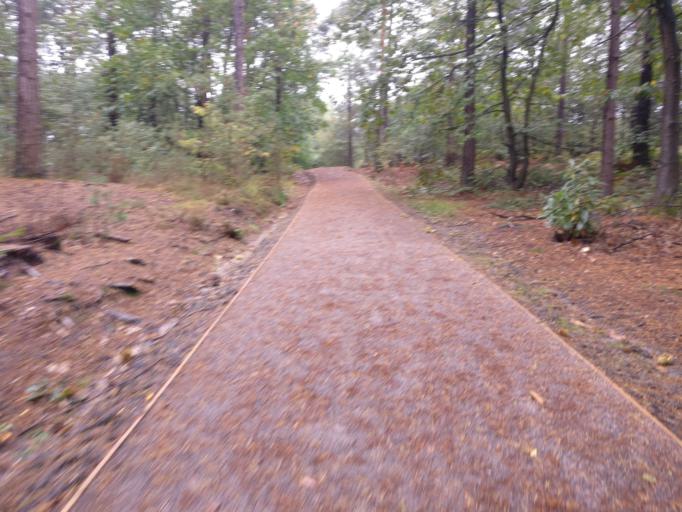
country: GB
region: England
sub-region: Surrey
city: Frimley
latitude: 51.3161
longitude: -0.7081
